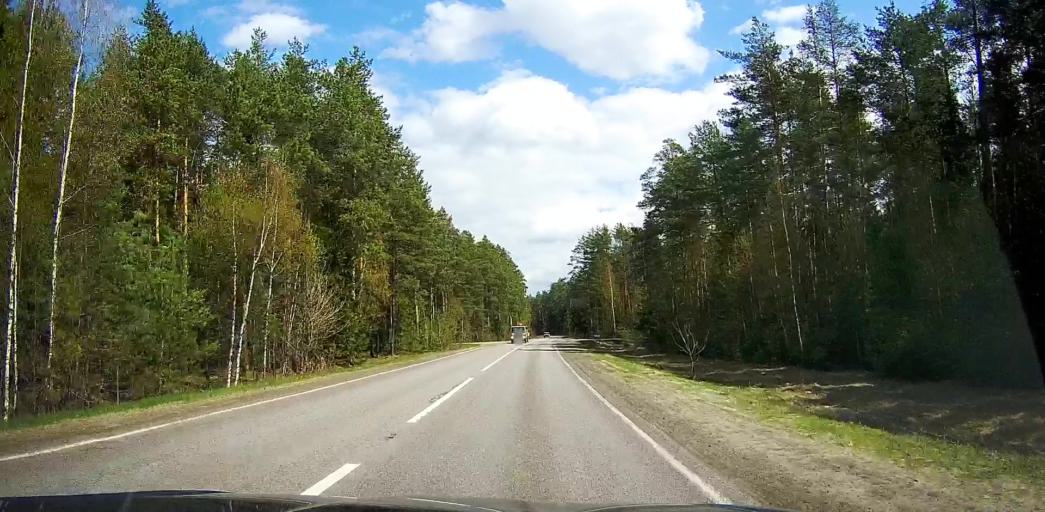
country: RU
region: Moskovskaya
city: Davydovo
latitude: 55.5578
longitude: 38.8343
